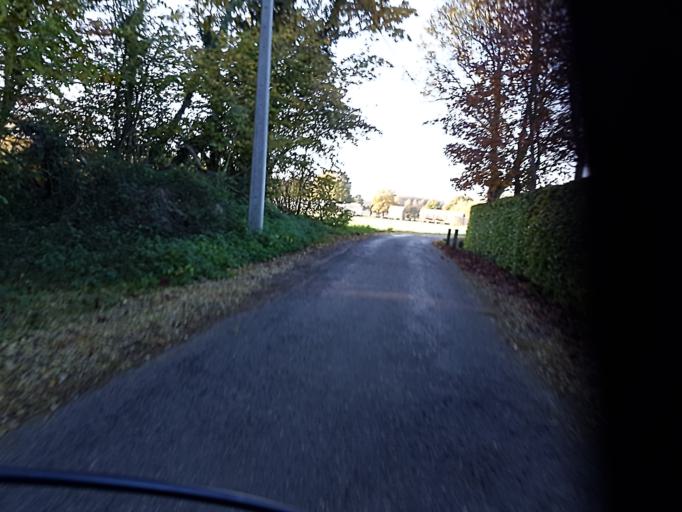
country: BE
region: Flanders
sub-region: Provincie Antwerpen
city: Bonheiden
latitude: 51.0323
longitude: 4.5588
